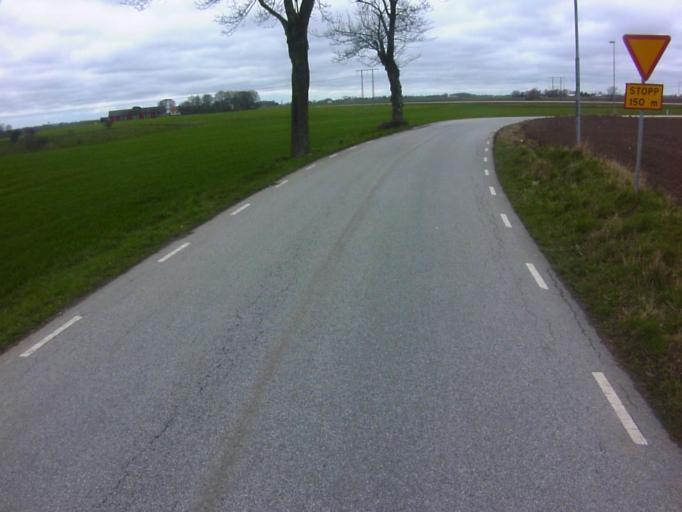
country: SE
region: Skane
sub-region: Kavlinge Kommun
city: Kaevlinge
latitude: 55.7955
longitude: 13.1908
